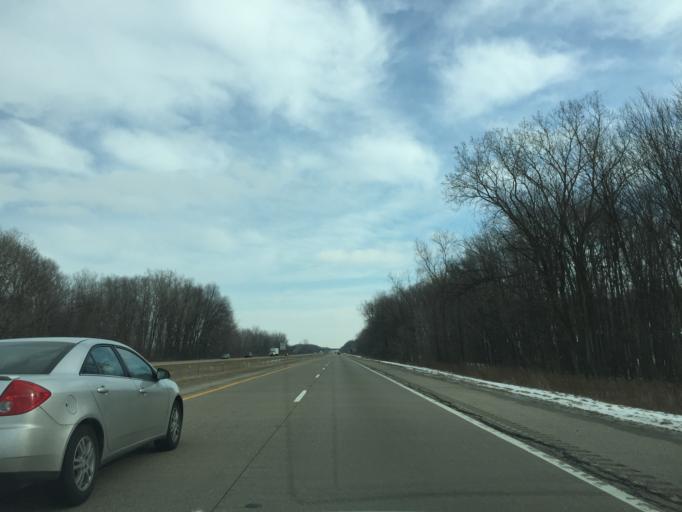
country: US
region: Michigan
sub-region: Ionia County
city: Saranac
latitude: 42.8792
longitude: -85.2247
